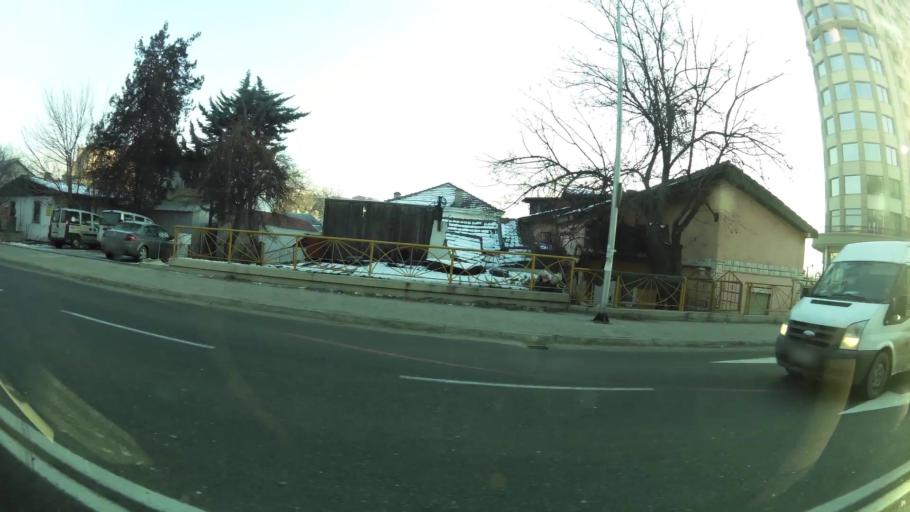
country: MK
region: Karpos
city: Skopje
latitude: 41.9860
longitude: 21.4377
